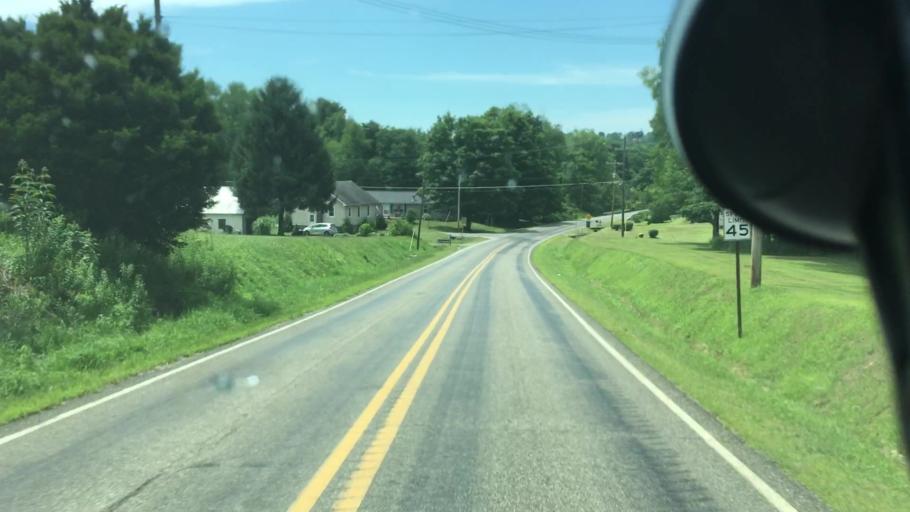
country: US
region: Pennsylvania
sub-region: Mercer County
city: Mercer
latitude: 41.2251
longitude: -80.2142
